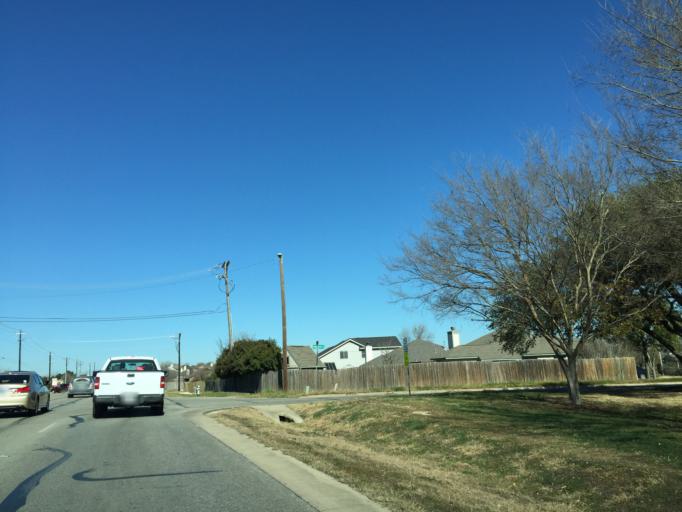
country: US
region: Texas
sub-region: Williamson County
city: Leander
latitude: 30.5595
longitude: -97.8610
